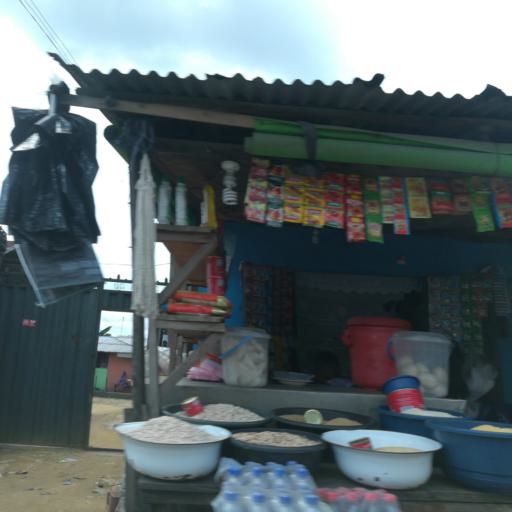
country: NG
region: Rivers
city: Port Harcourt
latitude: 4.7772
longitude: 7.0415
